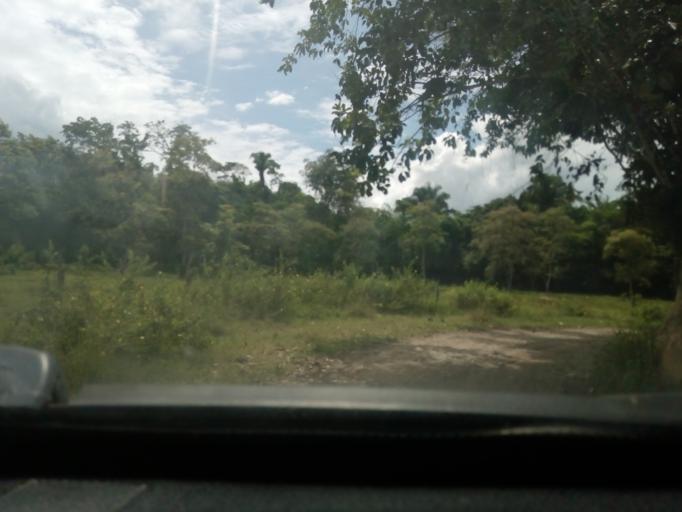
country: CO
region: Boyaca
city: Puerto Boyaca
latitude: 6.0107
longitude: -74.3868
